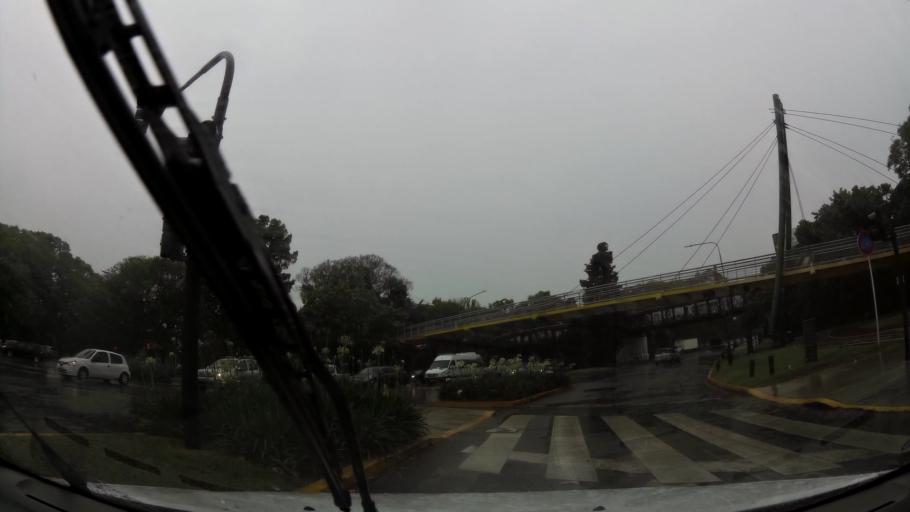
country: AR
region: Buenos Aires F.D.
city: Colegiales
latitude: -34.5655
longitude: -58.4203
